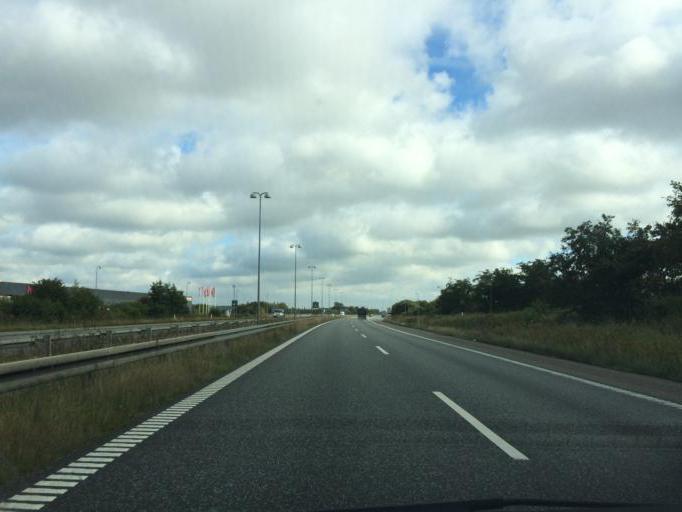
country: DK
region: North Denmark
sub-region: Alborg Kommune
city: Vestbjerg
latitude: 57.0872
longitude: 9.9761
